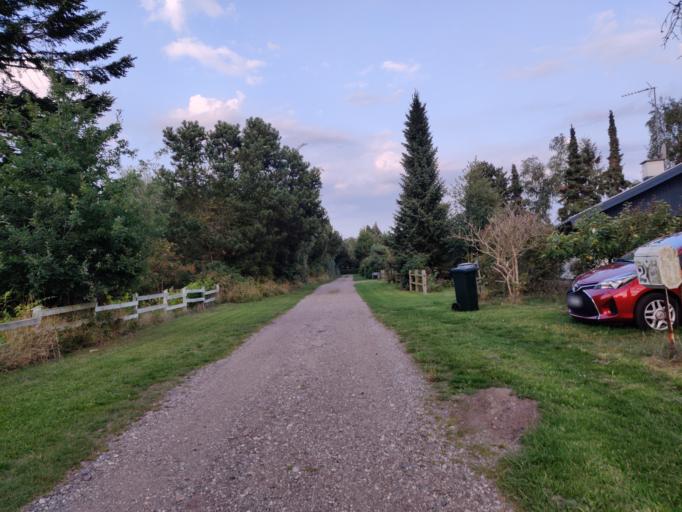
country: DK
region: Zealand
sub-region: Guldborgsund Kommune
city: Nykobing Falster
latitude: 54.5896
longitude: 11.9668
